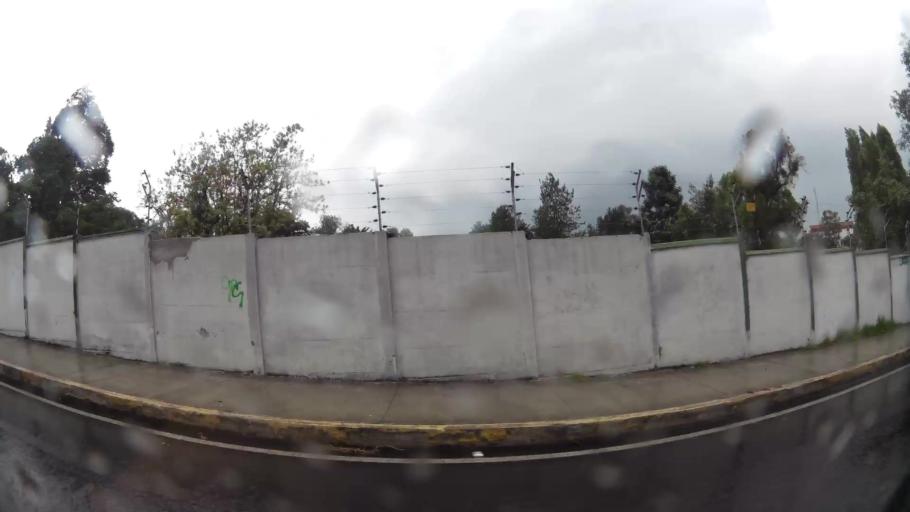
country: EC
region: Pichincha
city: Sangolqui
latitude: -0.3110
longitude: -78.4496
